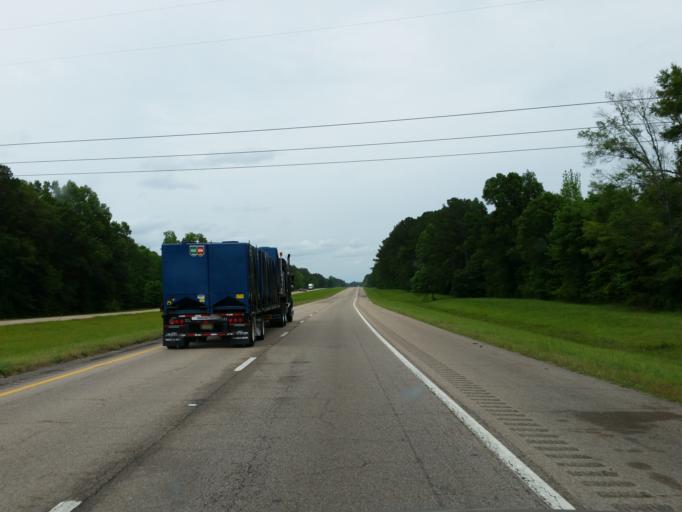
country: US
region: Mississippi
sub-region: Clarke County
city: Stonewall
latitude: 31.9921
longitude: -88.9446
